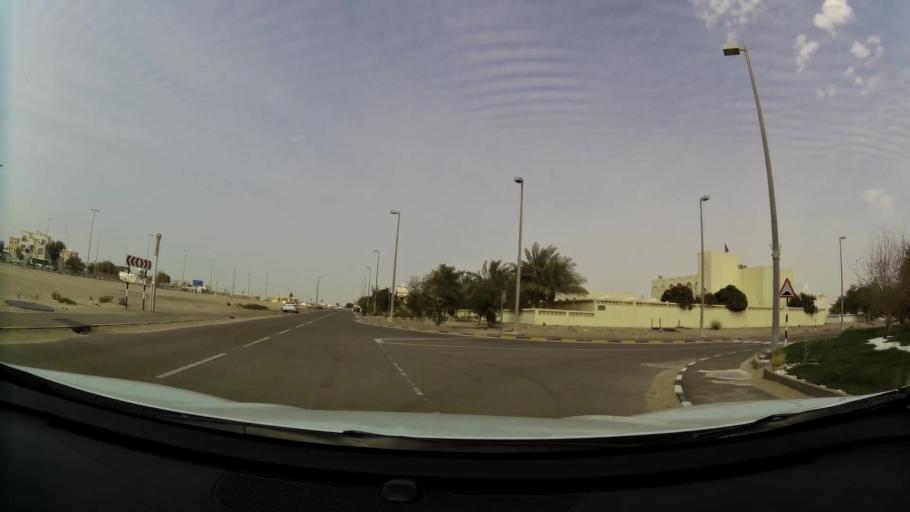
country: AE
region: Abu Dhabi
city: Abu Dhabi
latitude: 24.5541
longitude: 54.6861
